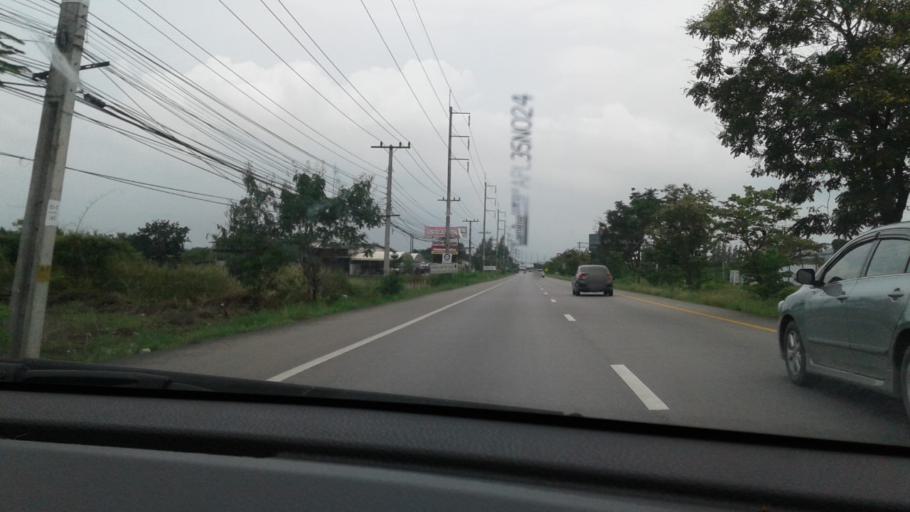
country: TH
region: Prachuap Khiri Khan
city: Prachuap Khiri Khan
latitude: 11.8349
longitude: 99.7814
